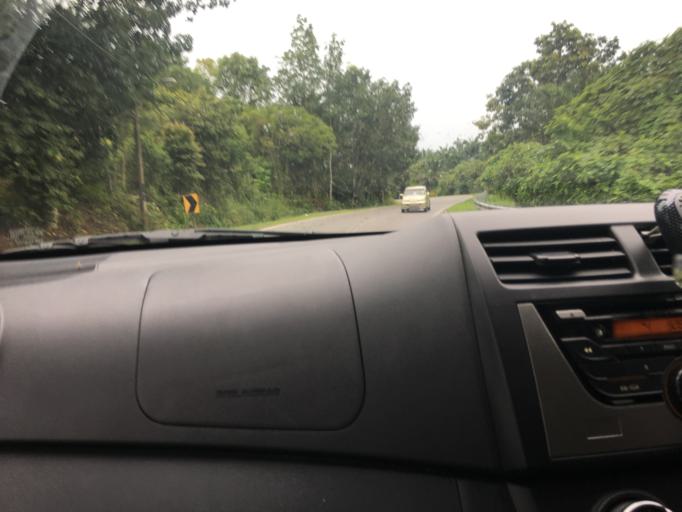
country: MY
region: Kedah
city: Bedong
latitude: 5.7096
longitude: 100.6320
